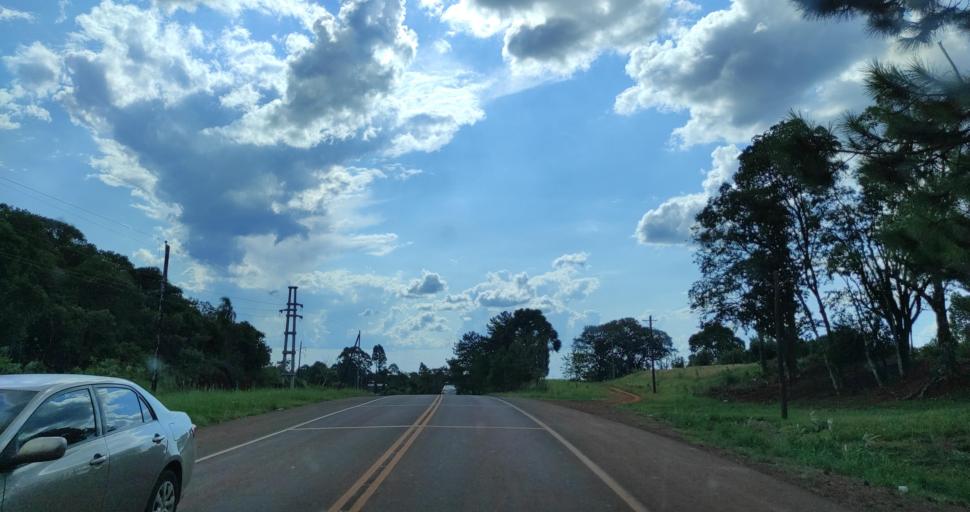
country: AR
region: Misiones
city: Bernardo de Irigoyen
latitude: -26.2928
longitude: -53.7669
